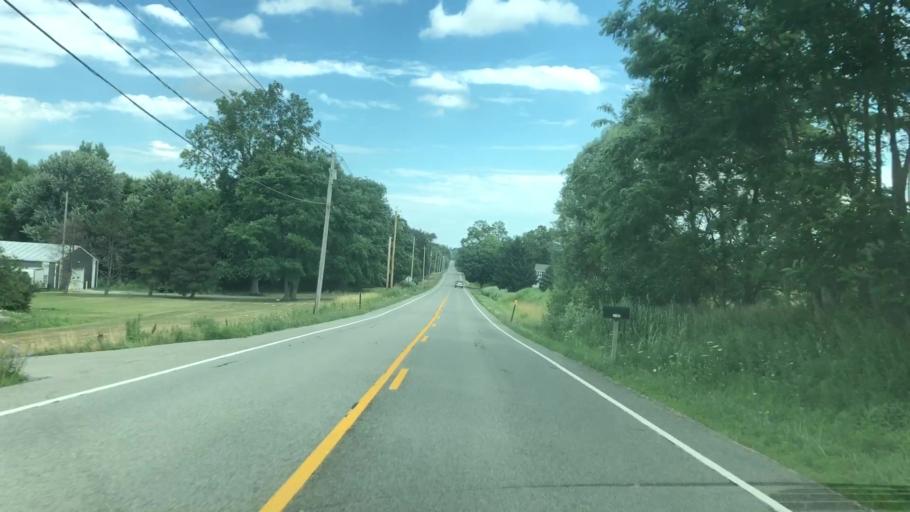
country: US
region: New York
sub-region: Wayne County
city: Macedon
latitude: 43.1062
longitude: -77.3523
